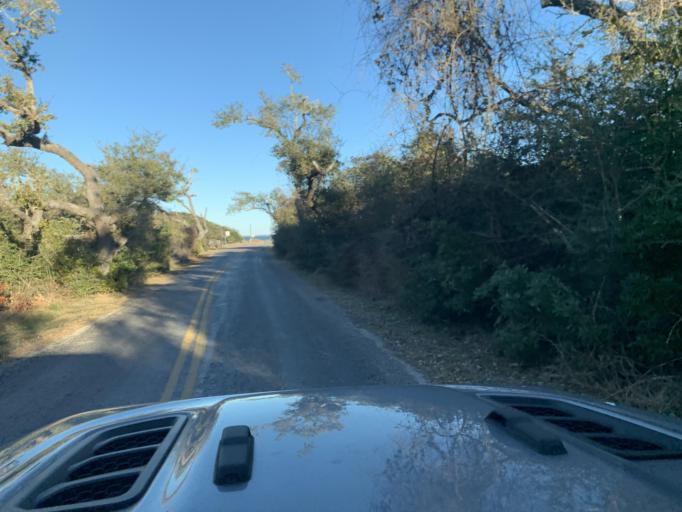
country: US
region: Texas
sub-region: Aransas County
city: Fulton
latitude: 28.1518
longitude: -96.9785
